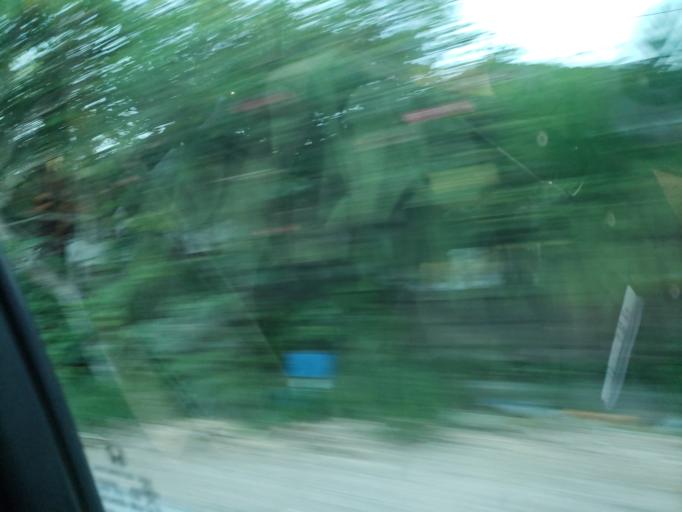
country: ID
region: Bali
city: Kangin
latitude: -8.8309
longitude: 115.1318
